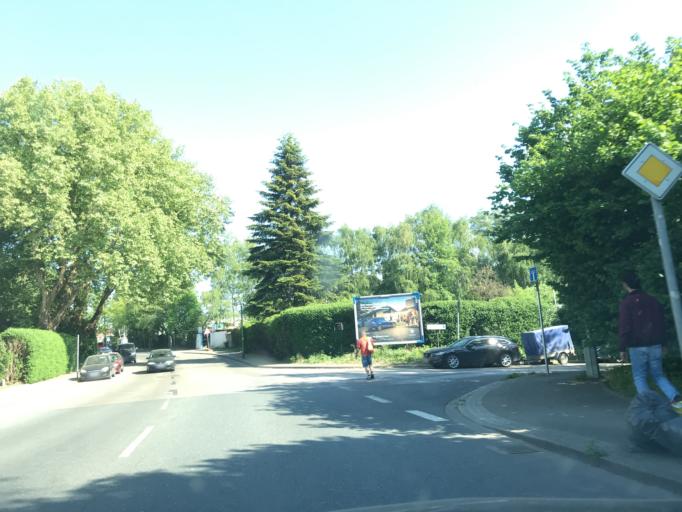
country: DE
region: North Rhine-Westphalia
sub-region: Regierungsbezirk Dusseldorf
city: Essen
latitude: 51.4681
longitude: 7.0726
